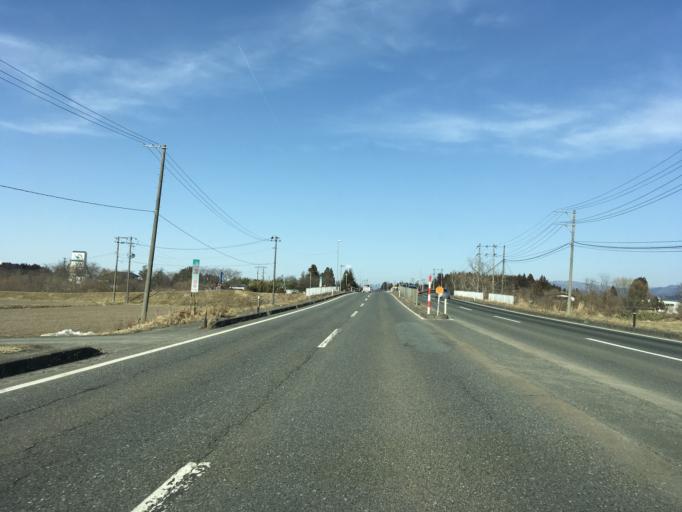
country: JP
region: Iwate
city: Hanamaki
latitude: 39.5194
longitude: 141.1605
